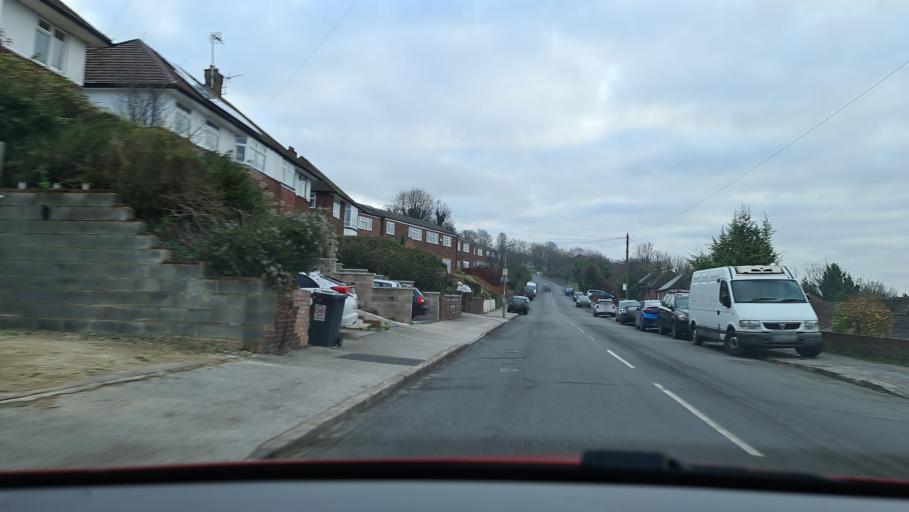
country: GB
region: England
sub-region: Buckinghamshire
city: High Wycombe
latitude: 51.6400
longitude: -0.7718
